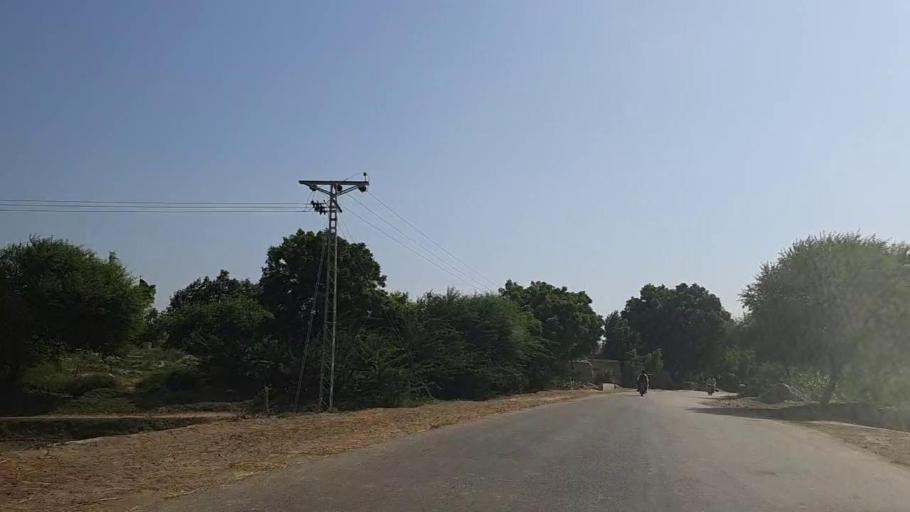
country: PK
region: Sindh
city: Daro Mehar
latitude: 24.7644
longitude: 68.2177
